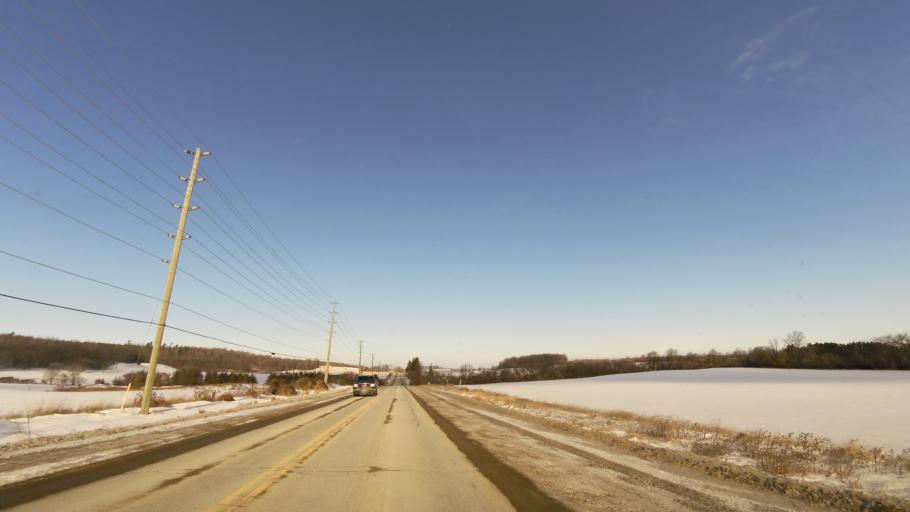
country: CA
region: Ontario
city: Quinte West
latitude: 44.1682
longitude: -77.8037
